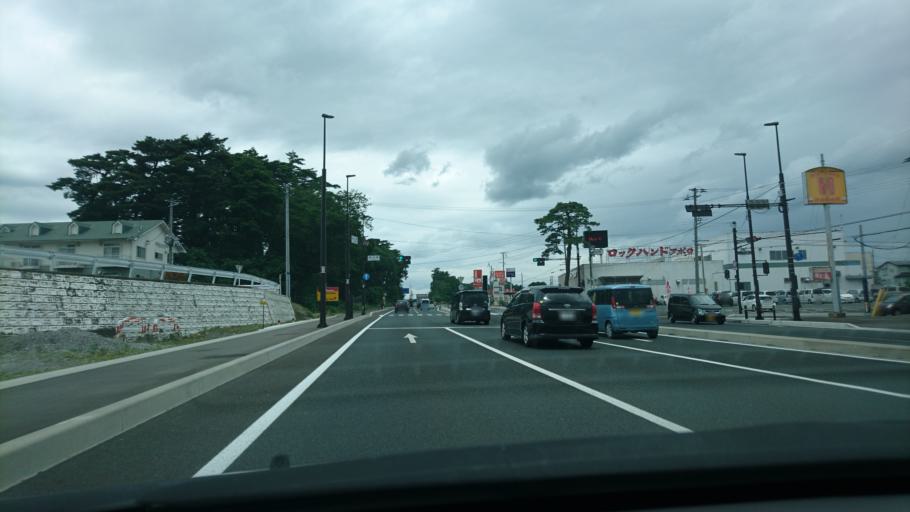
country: JP
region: Iwate
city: Morioka-shi
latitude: 39.7720
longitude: 141.1291
